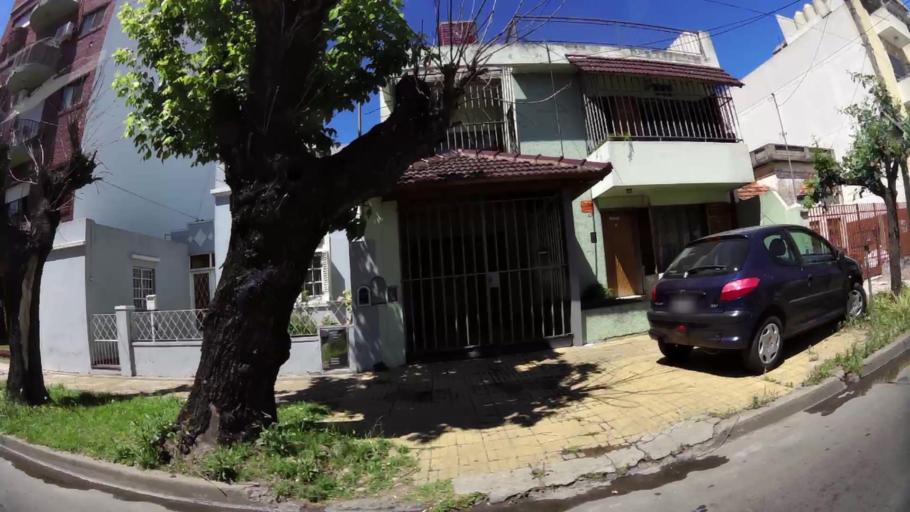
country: AR
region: Buenos Aires
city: Caseros
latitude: -34.6015
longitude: -58.5566
